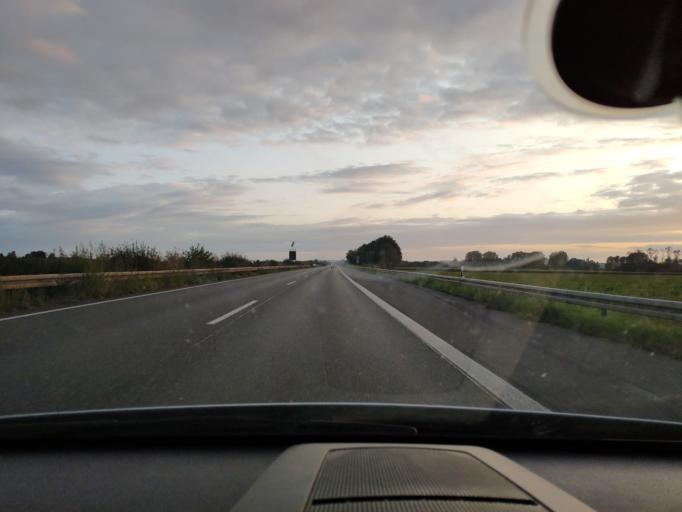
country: DE
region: North Rhine-Westphalia
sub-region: Regierungsbezirk Koln
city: Alsdorf
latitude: 50.8329
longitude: 6.1860
